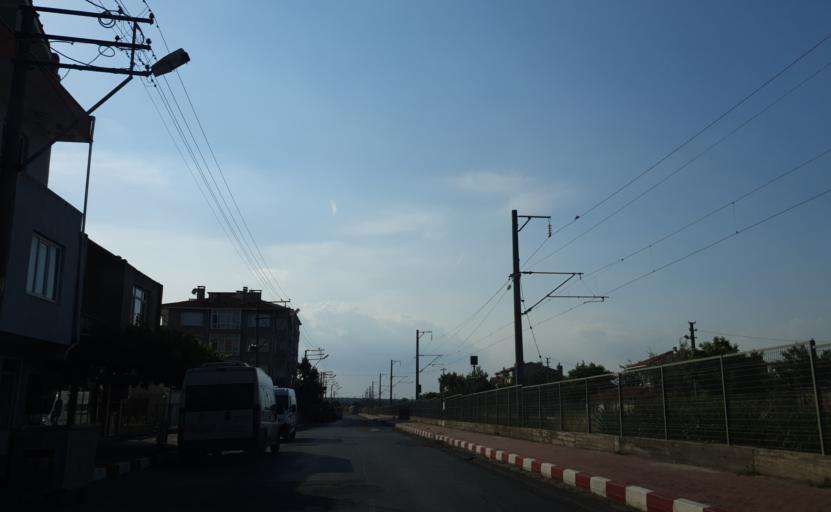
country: TR
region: Tekirdag
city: Muratli
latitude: 41.1760
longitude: 27.4918
